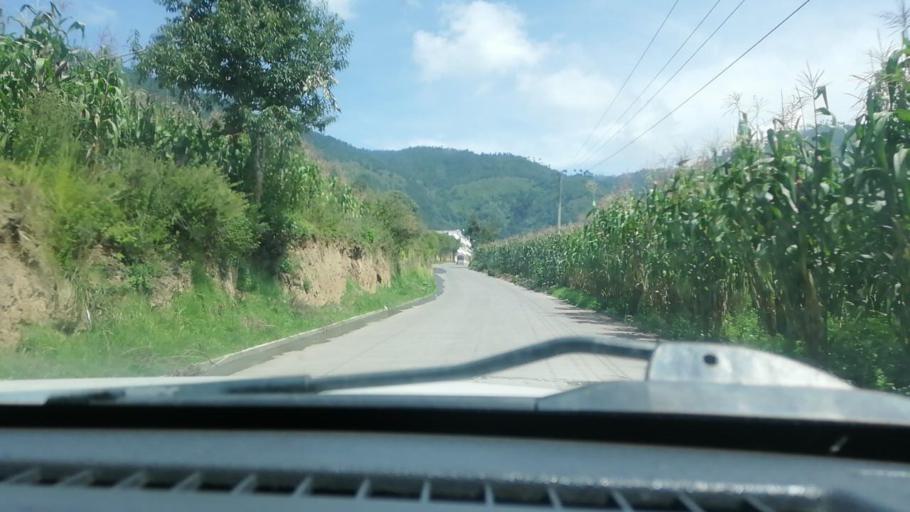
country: GT
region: Totonicapan
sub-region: Municipio de San Andres Xecul
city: San Andres Xecul
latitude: 14.8979
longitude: -91.4785
